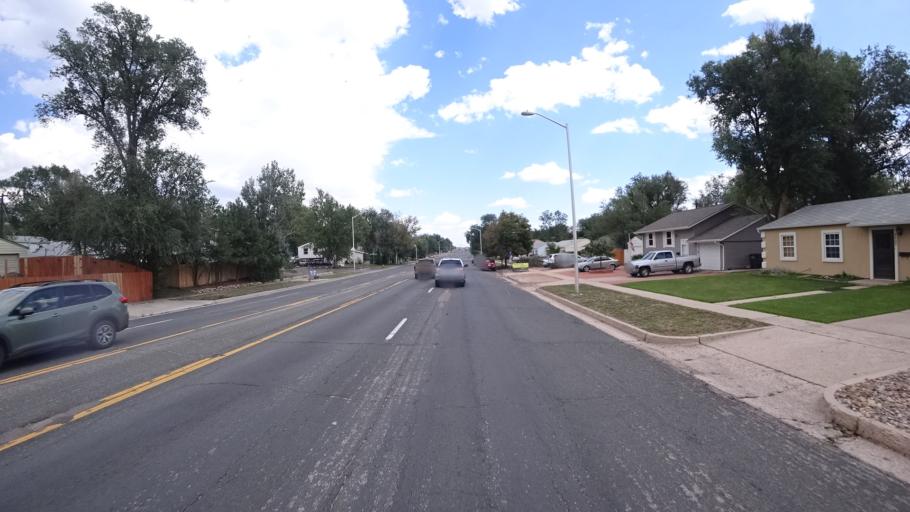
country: US
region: Colorado
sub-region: El Paso County
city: Colorado Springs
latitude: 38.8327
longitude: -104.7720
